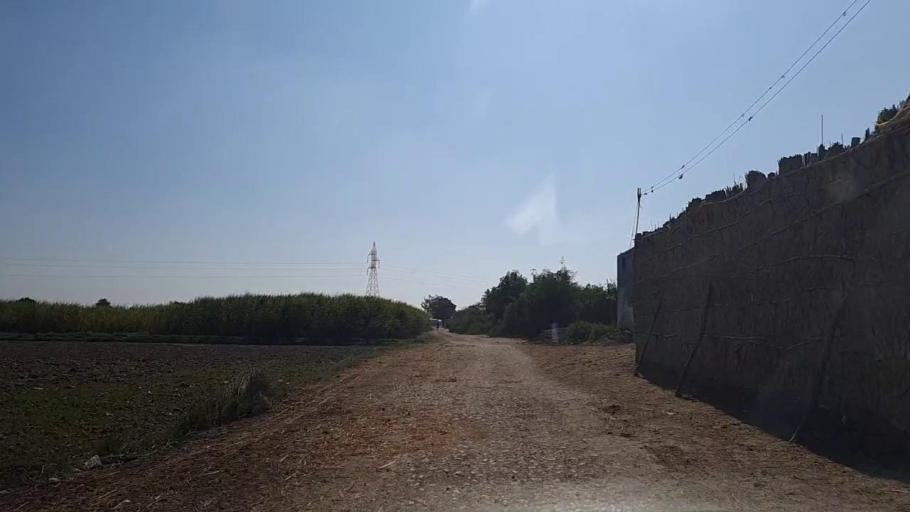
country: PK
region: Sindh
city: Mirpur Batoro
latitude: 24.6883
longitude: 68.1854
